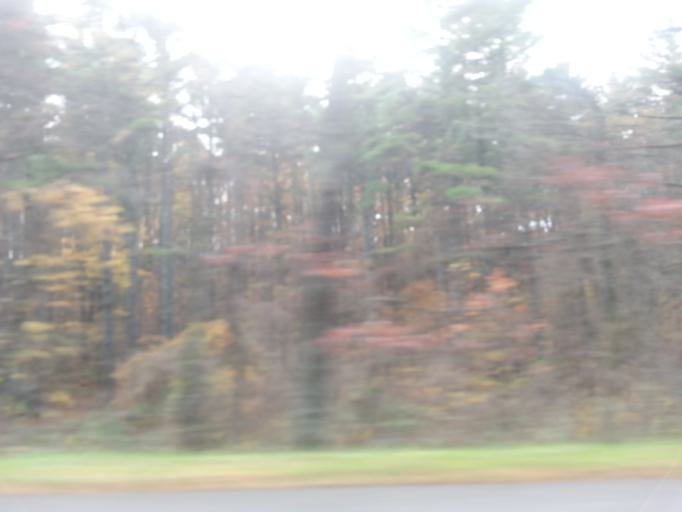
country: US
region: Virginia
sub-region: City of Galax
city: Galax
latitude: 36.5702
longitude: -80.8869
